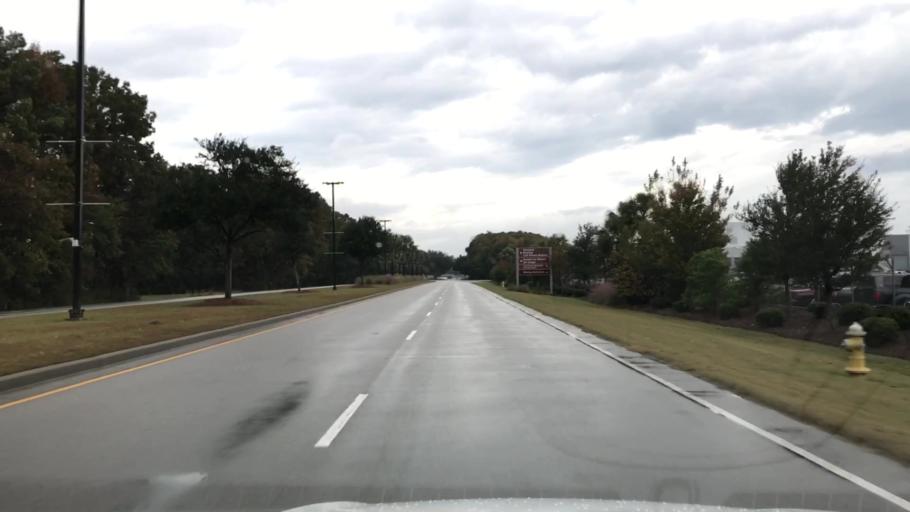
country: US
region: South Carolina
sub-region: Berkeley County
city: Hanahan
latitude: 32.8759
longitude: -80.0376
